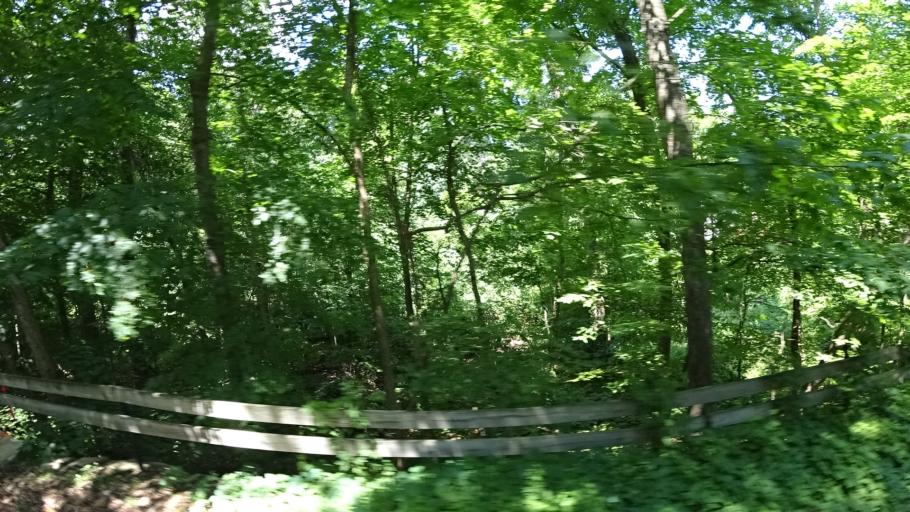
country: US
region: Massachusetts
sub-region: Norfolk County
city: Dedham
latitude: 42.2512
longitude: -71.1942
